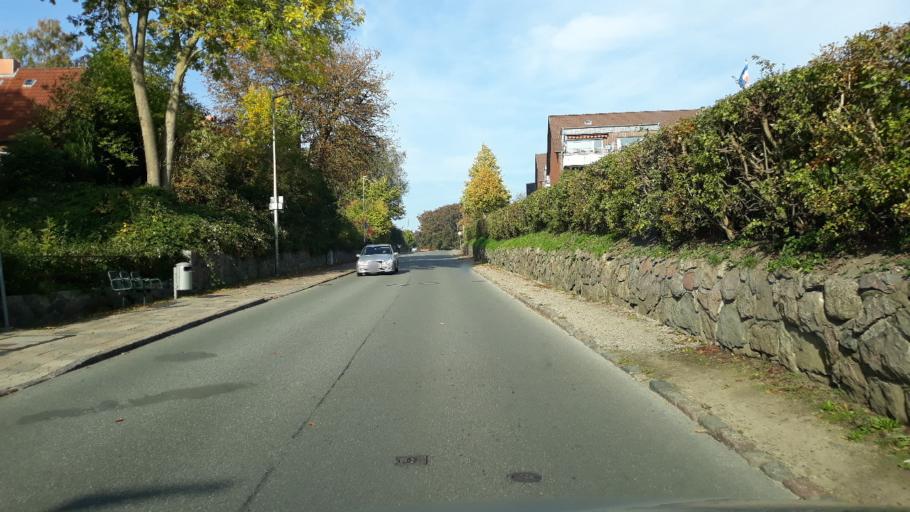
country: DE
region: Schleswig-Holstein
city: Schleswig
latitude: 54.5198
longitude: 9.5709
